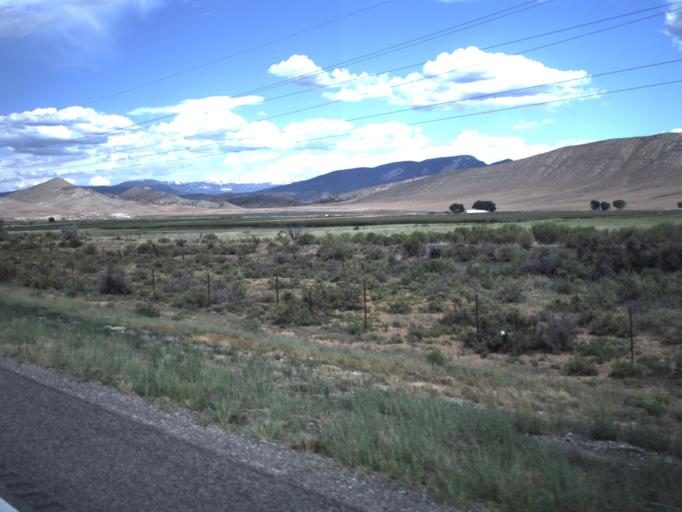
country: US
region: Utah
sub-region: Sevier County
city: Salina
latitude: 38.9921
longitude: -111.8464
